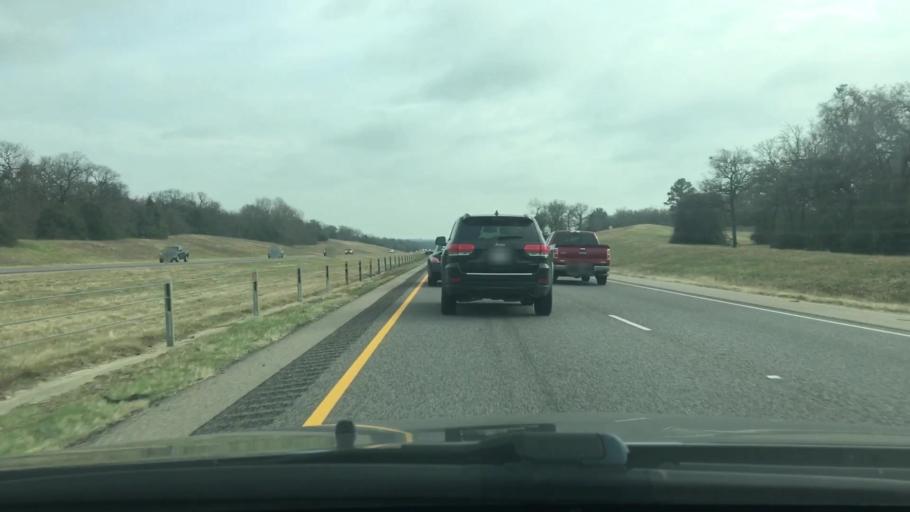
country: US
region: Texas
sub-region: Leon County
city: Buffalo
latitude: 31.5196
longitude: -96.1093
